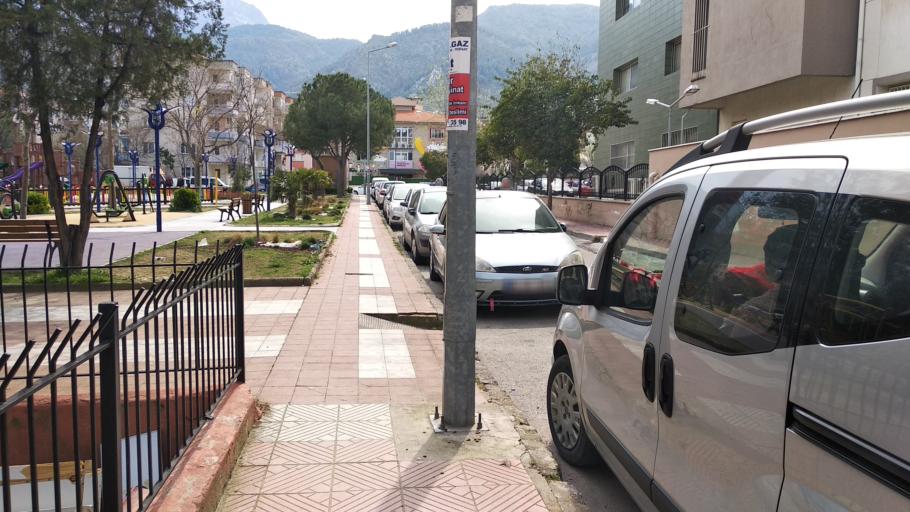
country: TR
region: Manisa
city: Manisa
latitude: 38.6156
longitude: 27.4179
